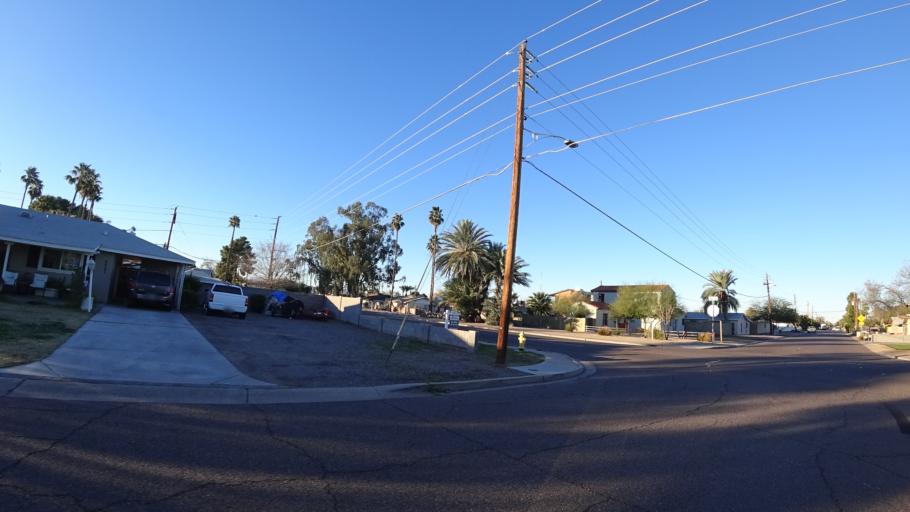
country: US
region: Arizona
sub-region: Maricopa County
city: Paradise Valley
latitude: 33.4841
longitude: -111.9952
